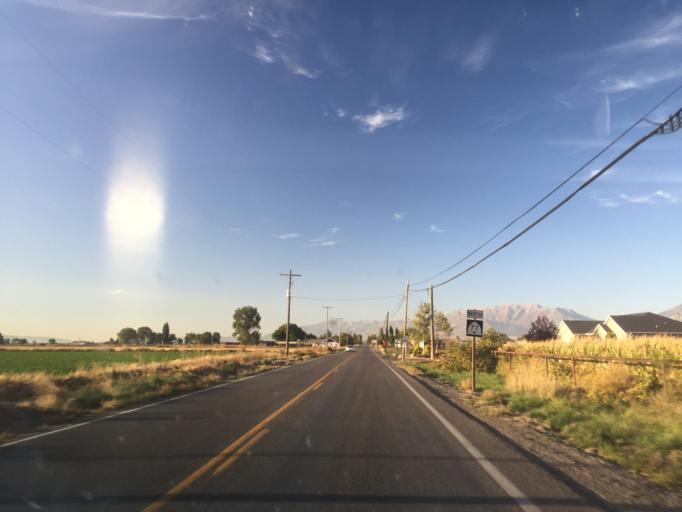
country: US
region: Utah
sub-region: Utah County
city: Benjamin
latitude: 40.1150
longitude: -111.7305
